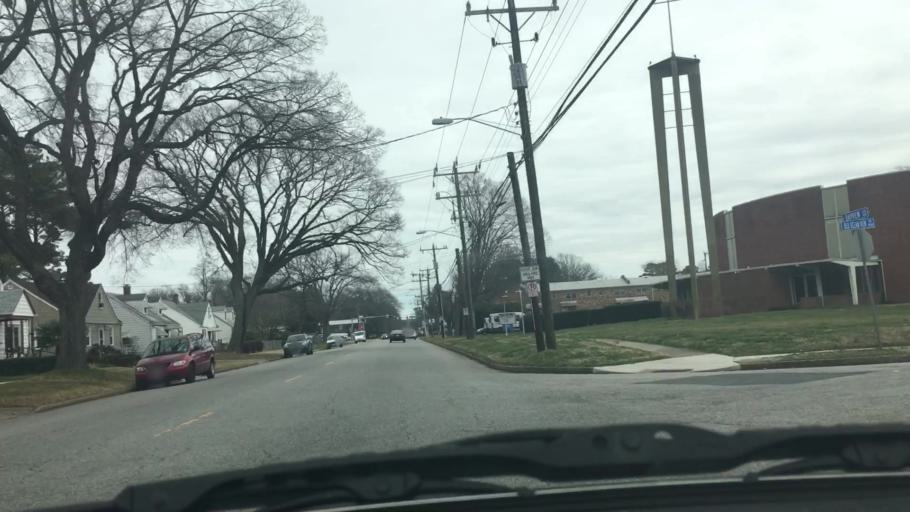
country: US
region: Virginia
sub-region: City of Norfolk
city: Norfolk
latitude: 36.9335
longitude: -76.2471
